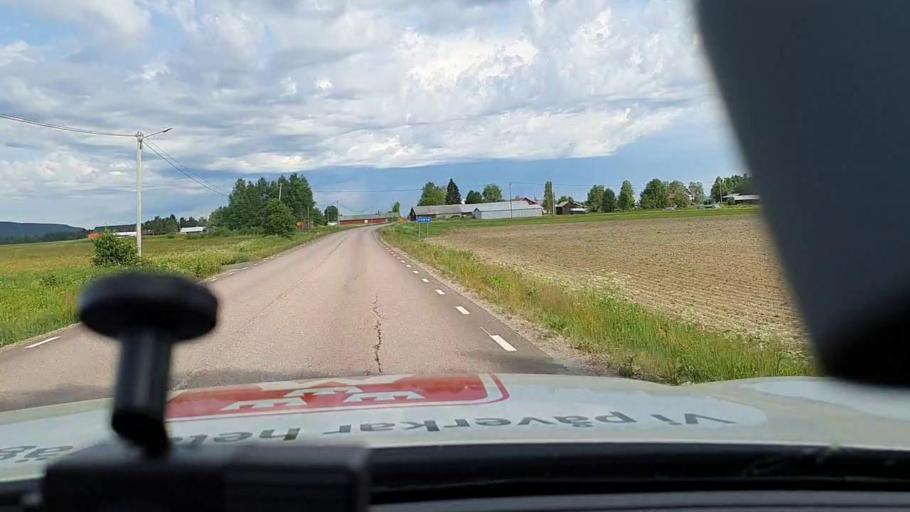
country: SE
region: Norrbotten
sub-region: Bodens Kommun
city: Saevast
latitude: 65.7010
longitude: 21.7710
